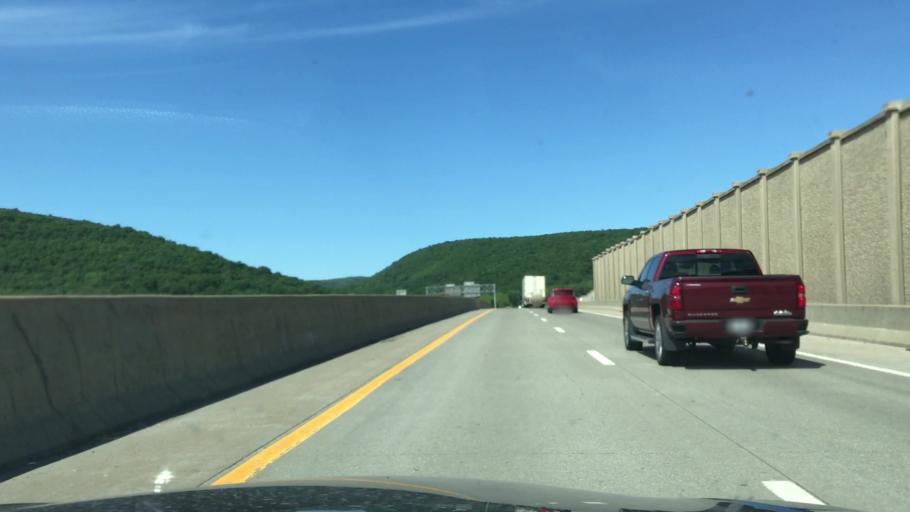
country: US
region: New York
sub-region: Steuben County
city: Painted Post
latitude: 42.1562
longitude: -77.0782
